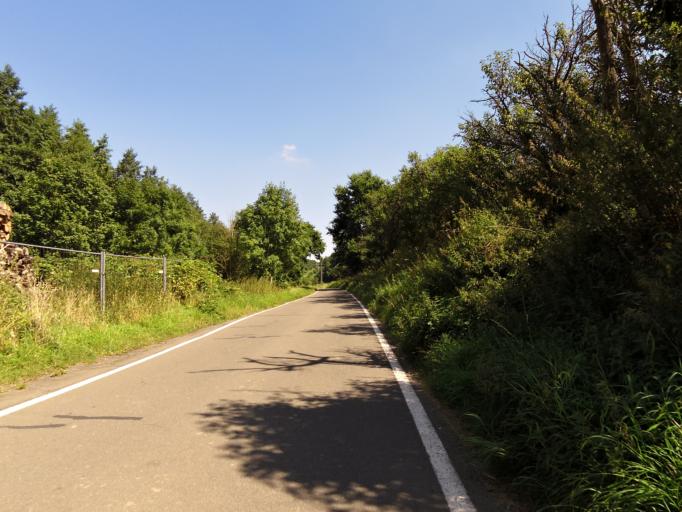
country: DE
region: Rheinland-Pfalz
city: Imsbach
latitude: 49.5827
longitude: 7.8885
